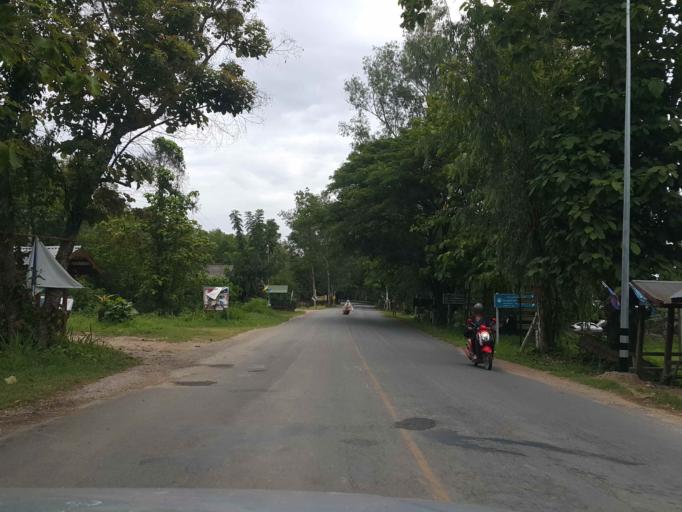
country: TH
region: Lampang
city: Thoen
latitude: 17.5960
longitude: 99.3318
